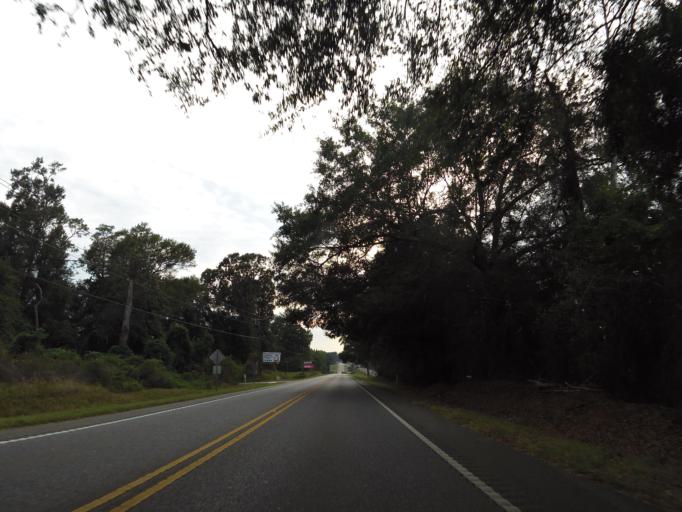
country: US
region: Alabama
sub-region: Escambia County
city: Atmore
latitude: 31.0221
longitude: -87.5323
